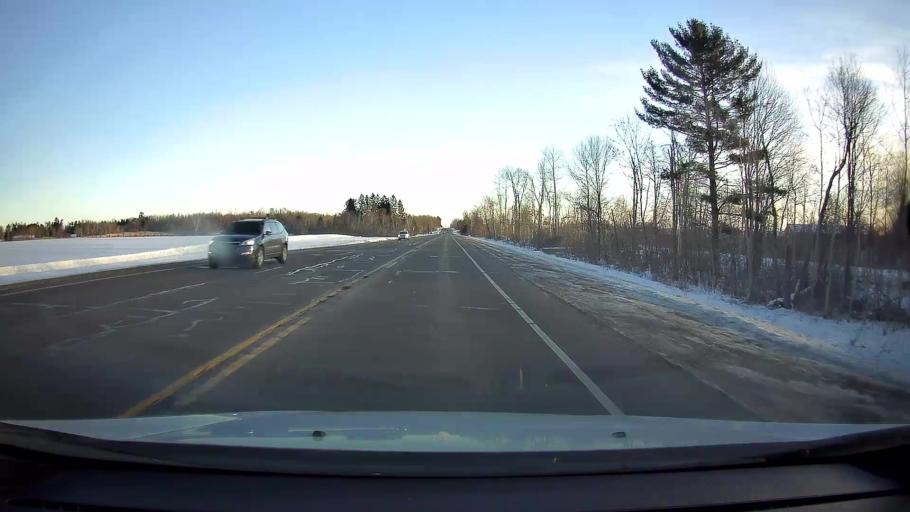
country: US
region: Wisconsin
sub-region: Barron County
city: Turtle Lake
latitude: 45.4636
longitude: -92.0964
